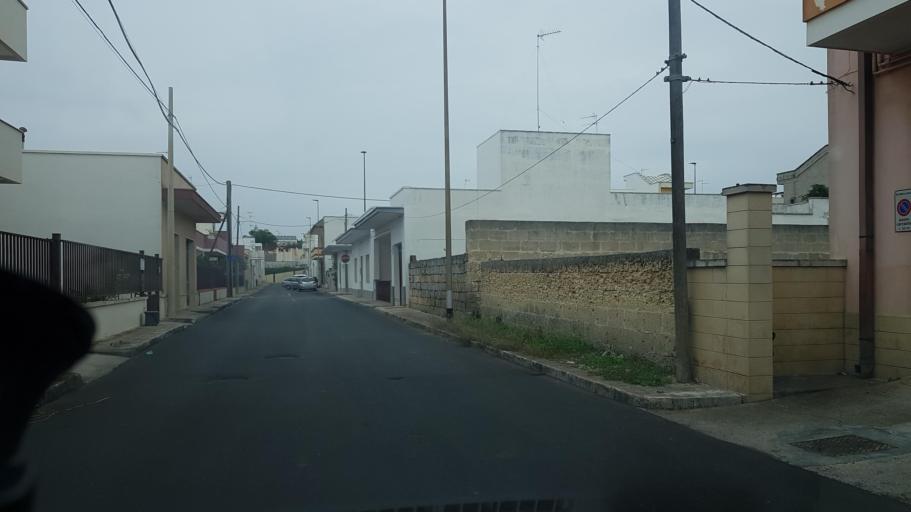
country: IT
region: Apulia
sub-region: Provincia di Lecce
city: Leverano
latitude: 40.2869
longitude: 18.0049
